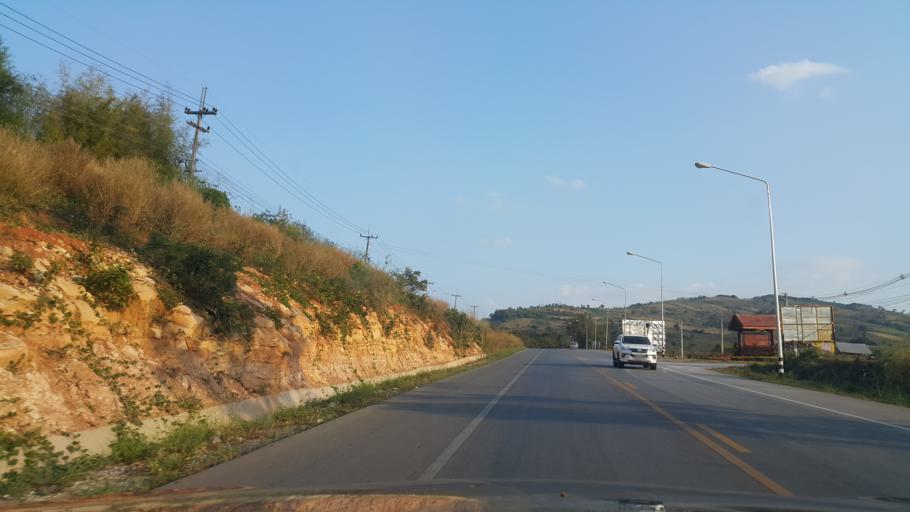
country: TH
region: Loei
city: Phu Ruea
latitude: 17.4511
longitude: 101.4226
